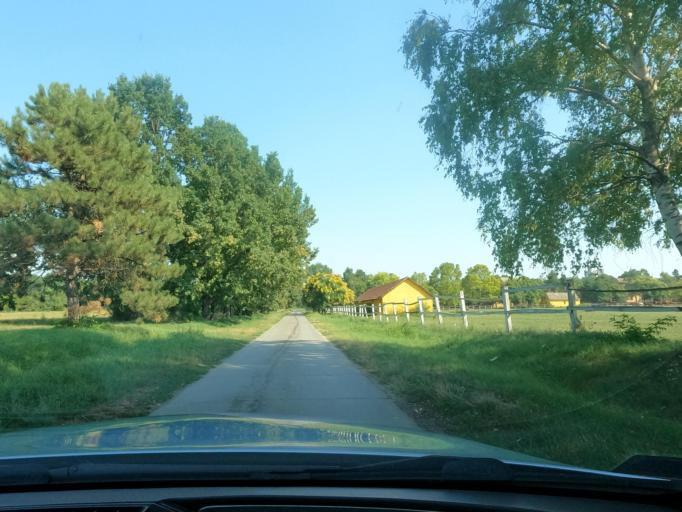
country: RS
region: Autonomna Pokrajina Vojvodina
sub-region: Juznobacki Okrug
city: Becej
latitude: 45.6552
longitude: 19.9001
